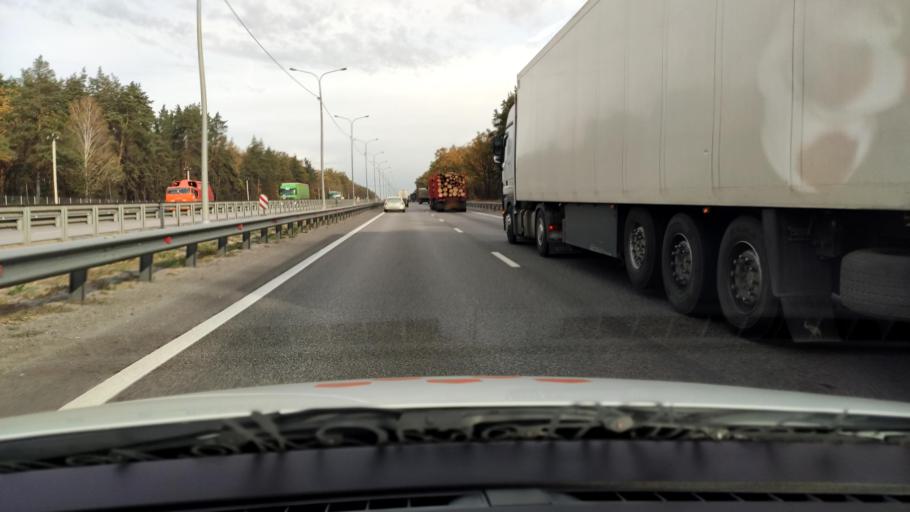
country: RU
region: Voronezj
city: Ramon'
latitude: 51.8715
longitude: 39.2166
